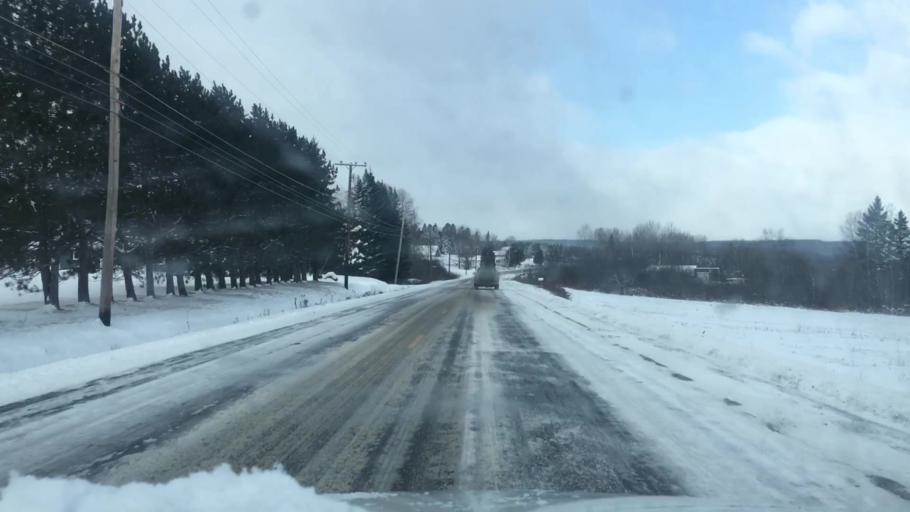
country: CA
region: New Brunswick
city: Harrison Brook
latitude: 47.2061
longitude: -67.9905
